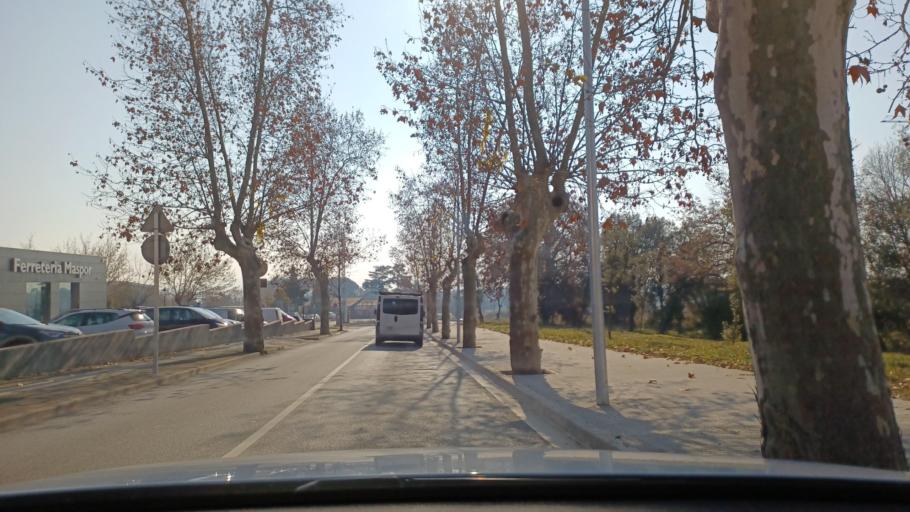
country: ES
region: Catalonia
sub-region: Provincia de Barcelona
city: L'Ametlla del Valles
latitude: 41.6642
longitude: 2.2665
